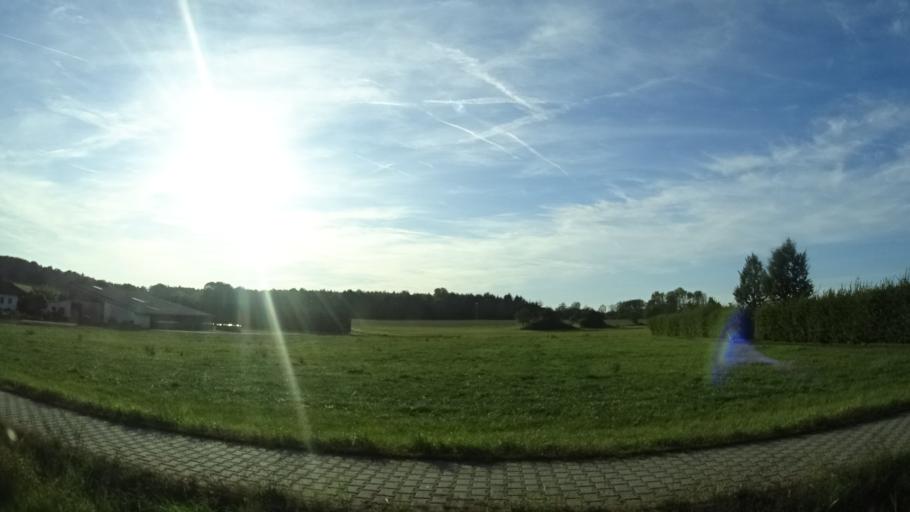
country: DE
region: Hesse
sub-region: Regierungsbezirk Darmstadt
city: Wachtersbach
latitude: 50.2902
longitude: 9.2623
